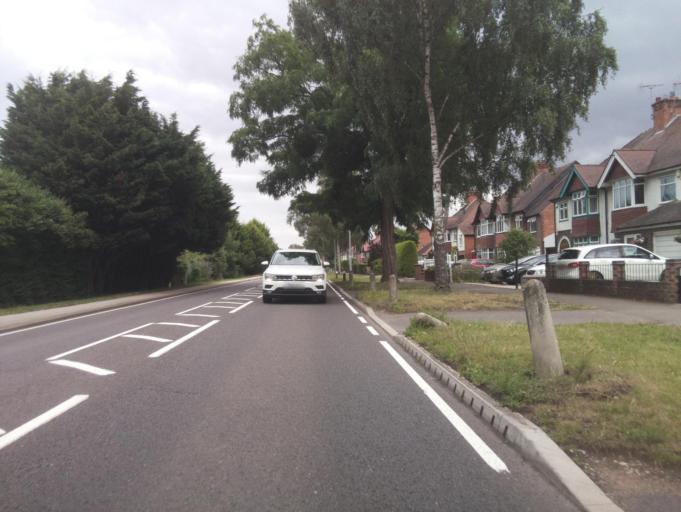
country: GB
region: England
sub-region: Nottinghamshire
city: Burton Joyce
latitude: 52.9894
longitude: -1.0319
